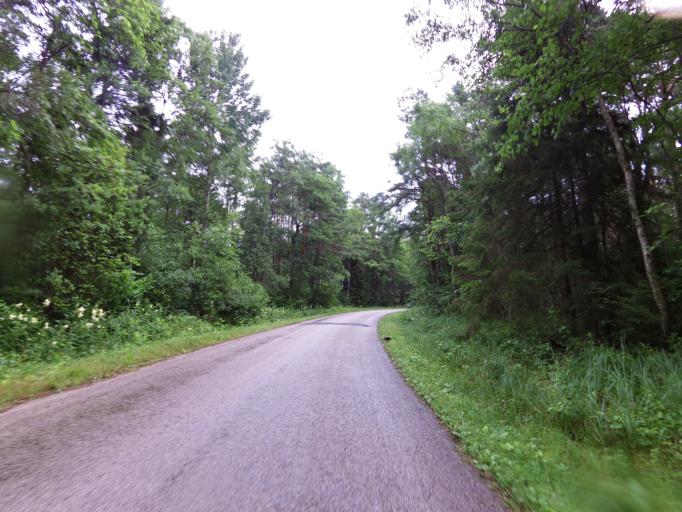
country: EE
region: Laeaene
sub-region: Vormsi vald
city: Hullo
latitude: 59.0036
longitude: 23.2555
